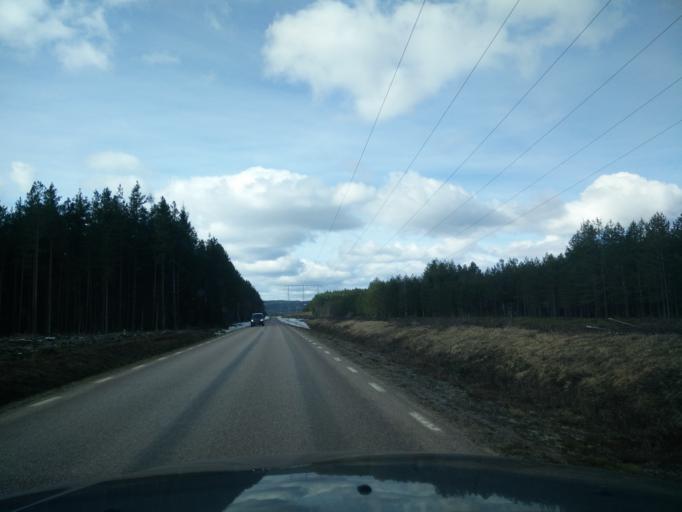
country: SE
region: Vaermland
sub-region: Hagfors Kommun
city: Hagfors
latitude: 60.0382
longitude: 13.5469
